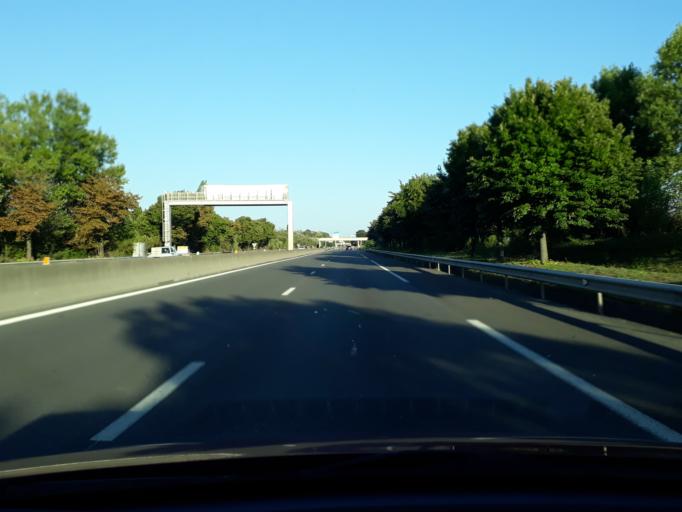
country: FR
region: Rhone-Alpes
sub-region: Departement du Rhone
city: Venissieux
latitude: 45.6847
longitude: 4.8795
